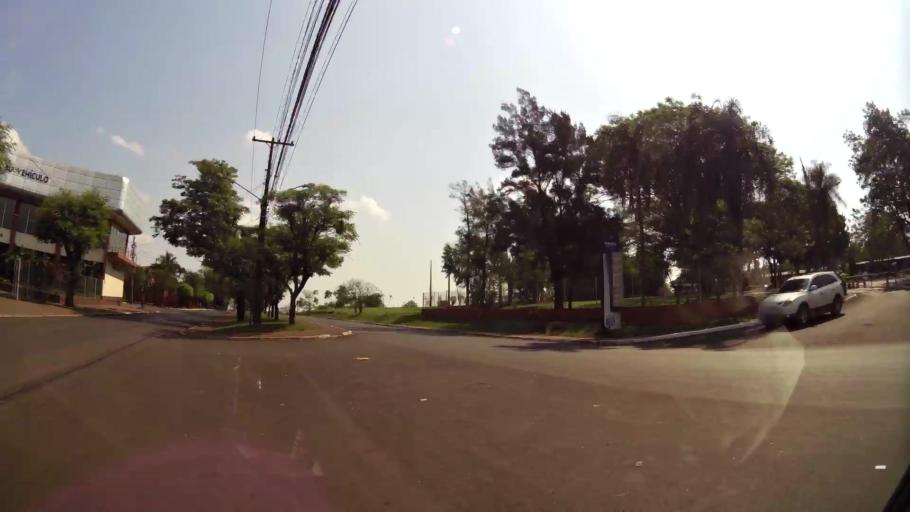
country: PY
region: Alto Parana
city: Ciudad del Este
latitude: -25.5112
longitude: -54.6296
